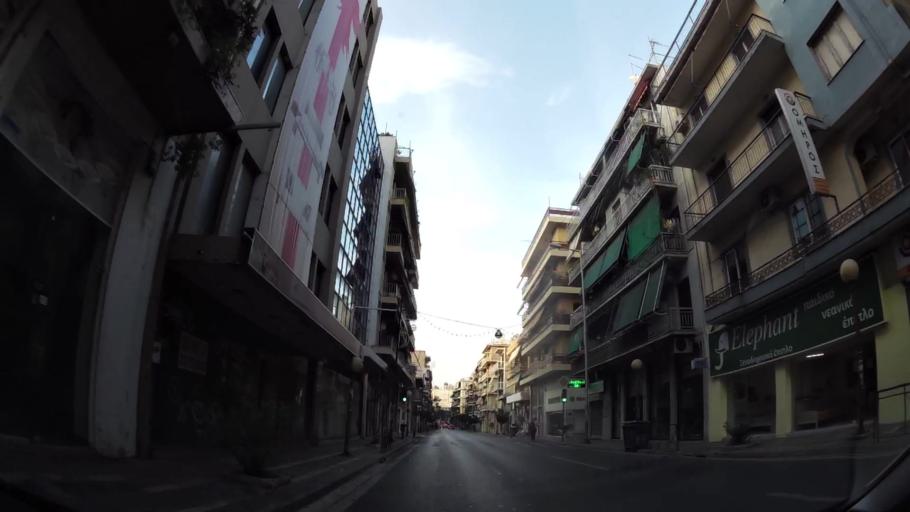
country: GR
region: Attica
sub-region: Nomarchia Athinas
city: Dhafni
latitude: 37.9552
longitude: 23.7388
